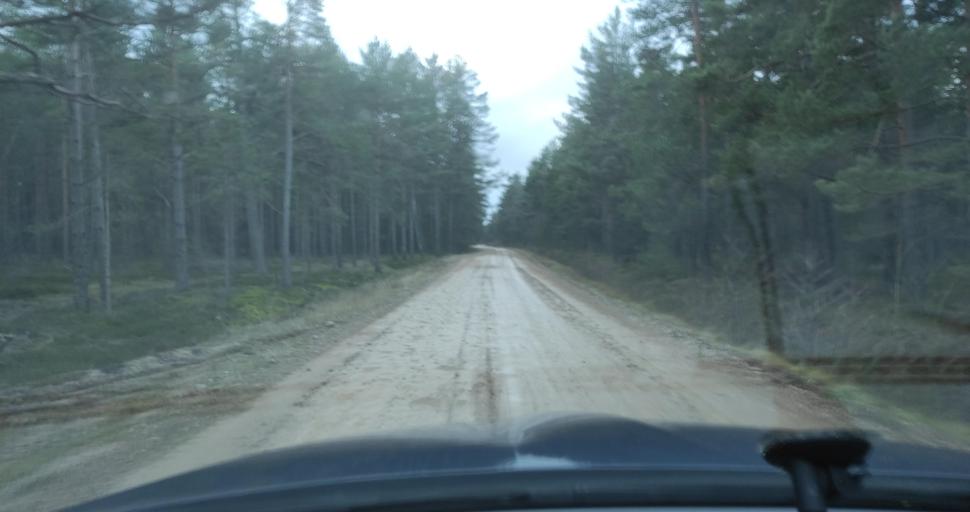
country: LV
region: Pavilostas
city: Pavilosta
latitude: 56.8336
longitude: 21.0740
